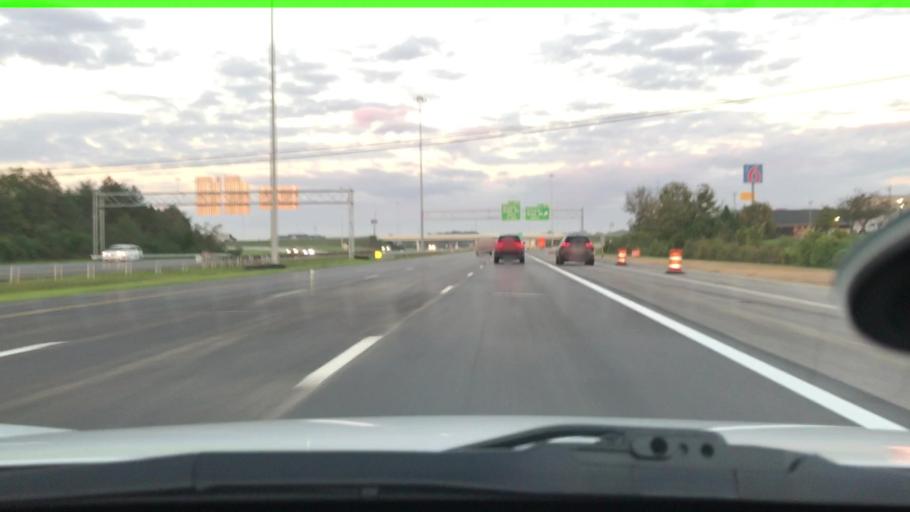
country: US
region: Ohio
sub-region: Franklin County
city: Lincoln Village
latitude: 39.9773
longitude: -83.1447
